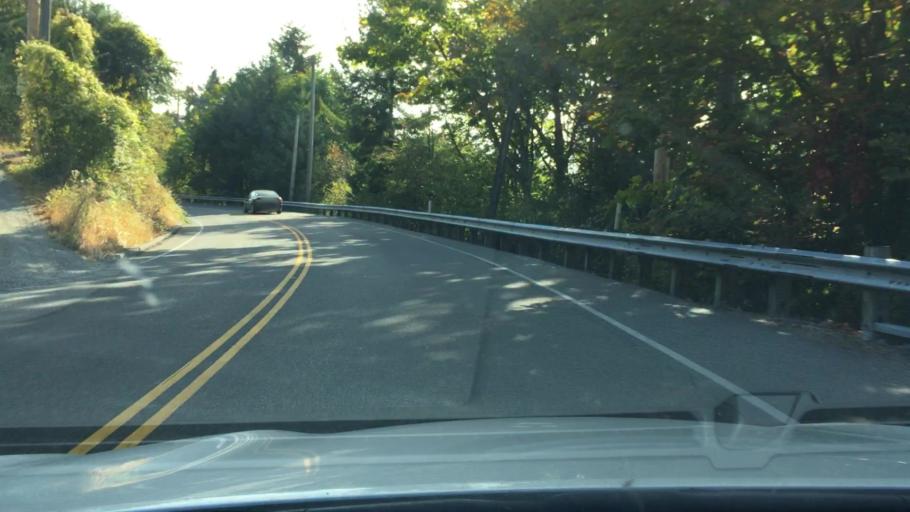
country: US
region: Washington
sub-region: Pierce County
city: Tacoma
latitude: 47.3071
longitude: -122.4335
